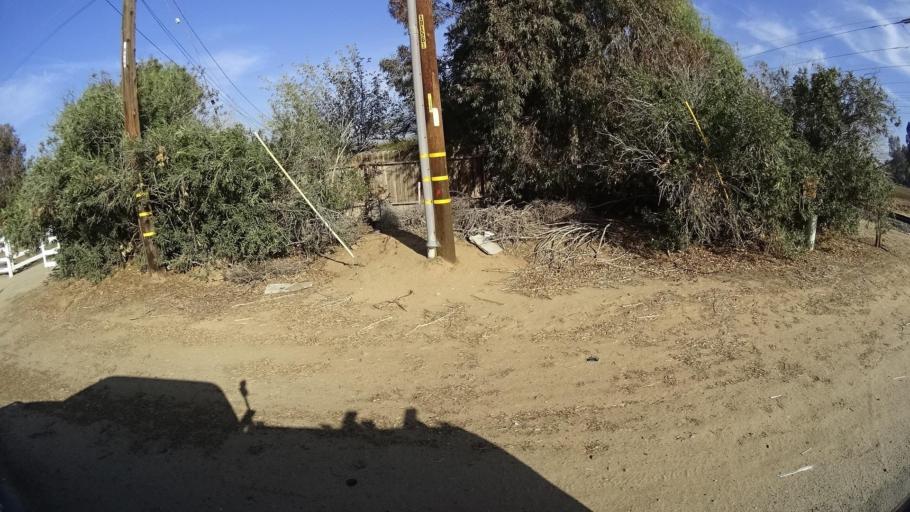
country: US
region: California
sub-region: Kern County
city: Lamont
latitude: 35.3253
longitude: -118.9235
